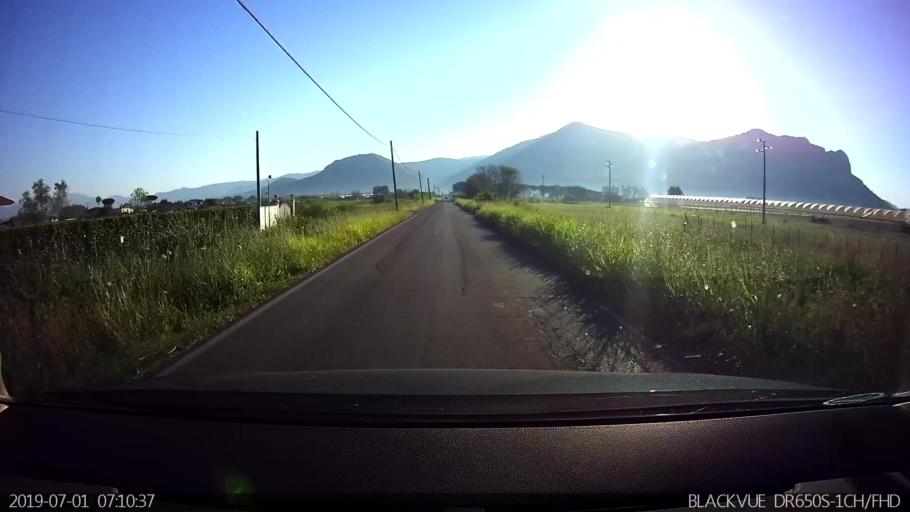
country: IT
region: Latium
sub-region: Provincia di Latina
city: Borgo Hermada
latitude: 41.3135
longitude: 13.1723
